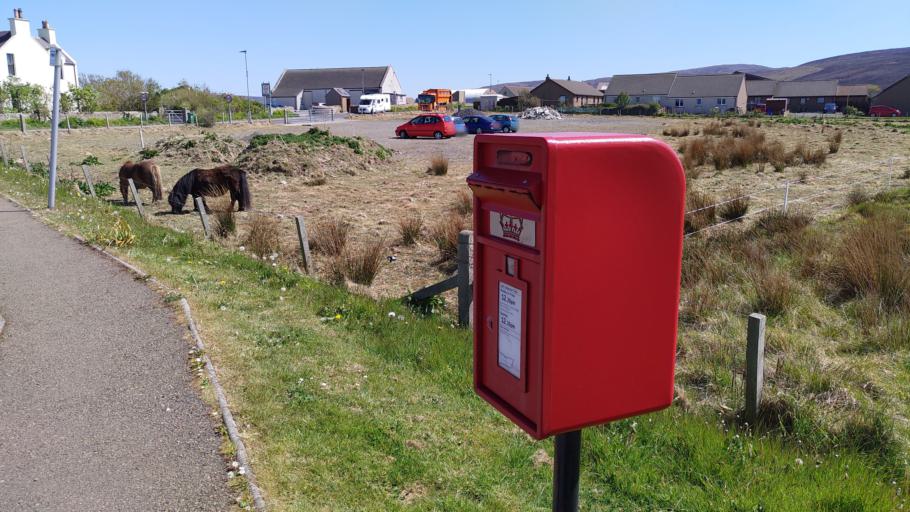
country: GB
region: Scotland
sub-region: Orkney Islands
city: Stromness
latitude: 58.9868
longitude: -3.2107
